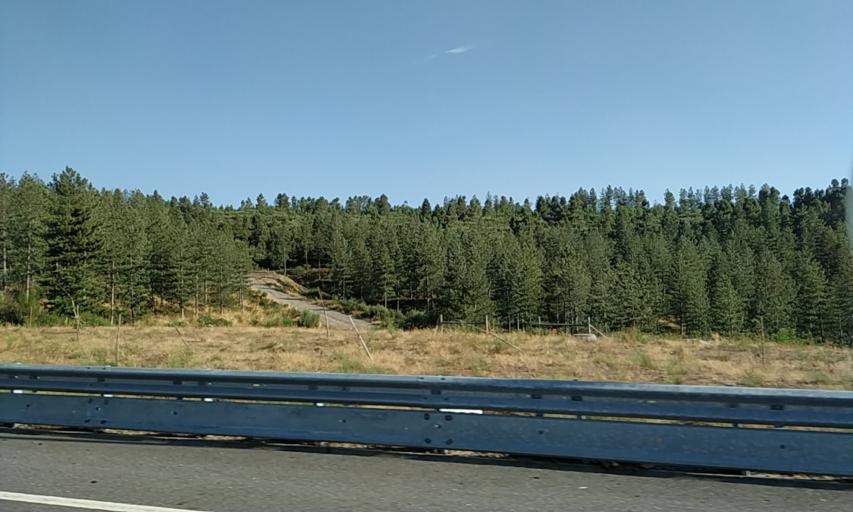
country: PT
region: Vila Real
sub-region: Santa Marta de Penaguiao
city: Santa Marta de Penaguiao
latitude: 41.2775
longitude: -7.8324
